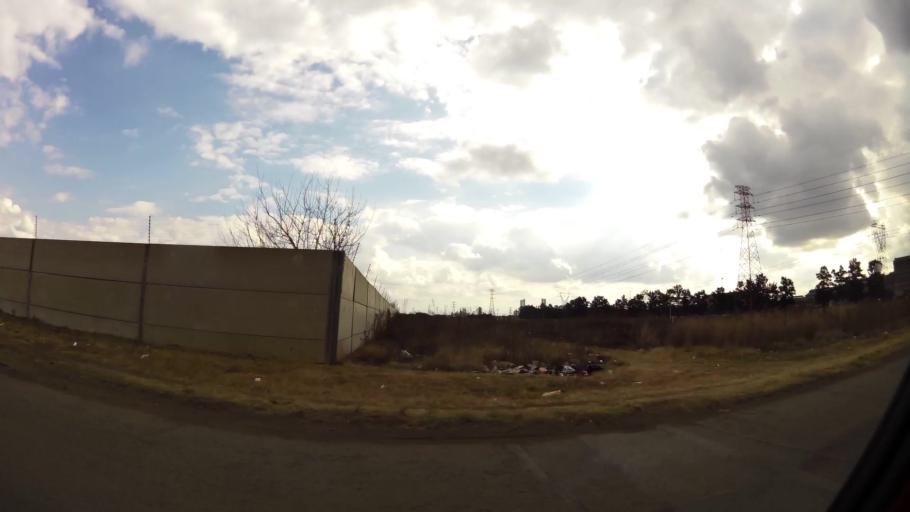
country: ZA
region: Gauteng
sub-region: Sedibeng District Municipality
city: Vanderbijlpark
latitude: -26.6738
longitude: 27.8182
